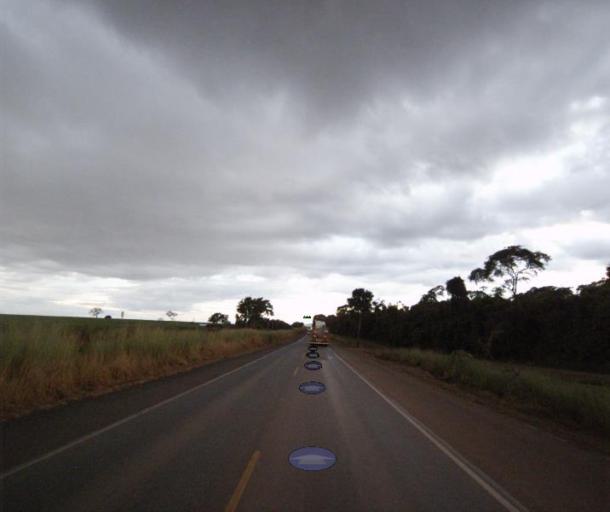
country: BR
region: Goias
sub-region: Uruacu
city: Uruacu
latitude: -14.6499
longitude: -49.1859
